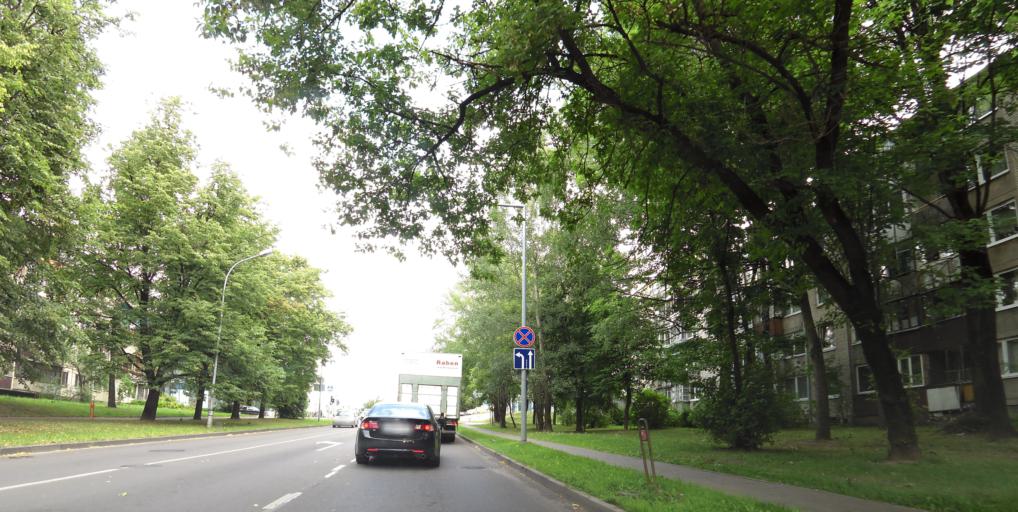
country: LT
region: Vilnius County
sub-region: Vilnius
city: Vilnius
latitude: 54.7069
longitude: 25.2905
